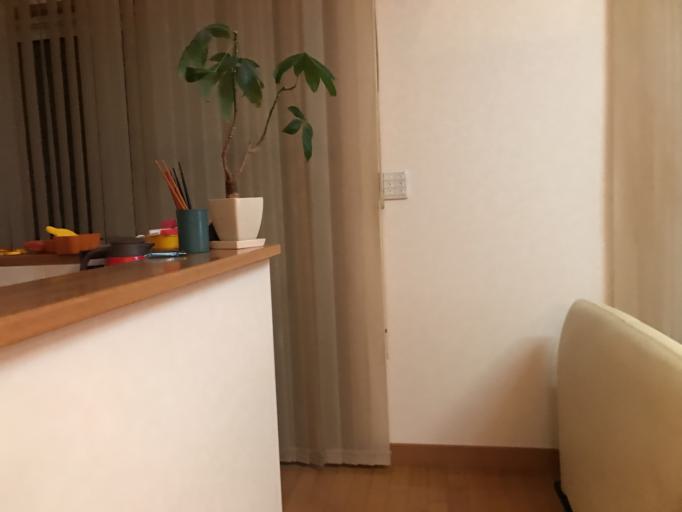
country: JP
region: Kanagawa
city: Kamakura
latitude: 35.3930
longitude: 139.5544
